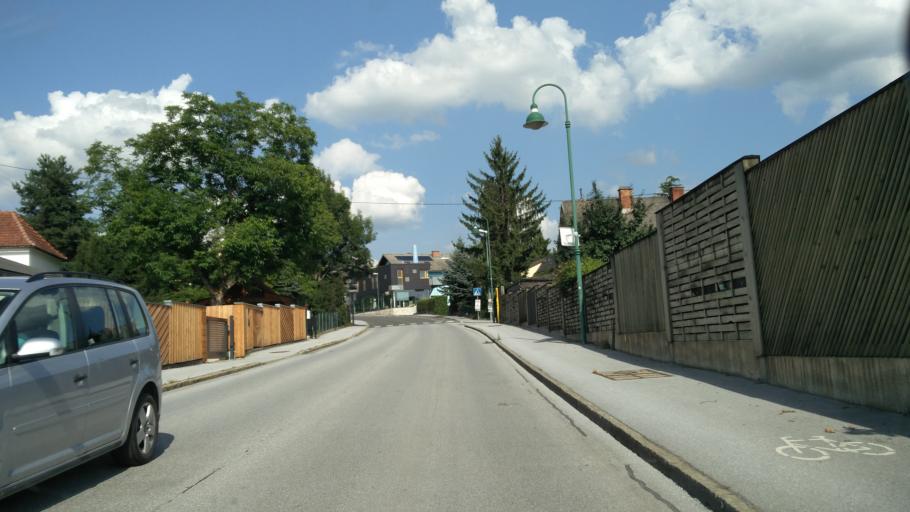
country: AT
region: Styria
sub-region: Politischer Bezirk Weiz
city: Weiz
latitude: 47.2195
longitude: 15.6358
